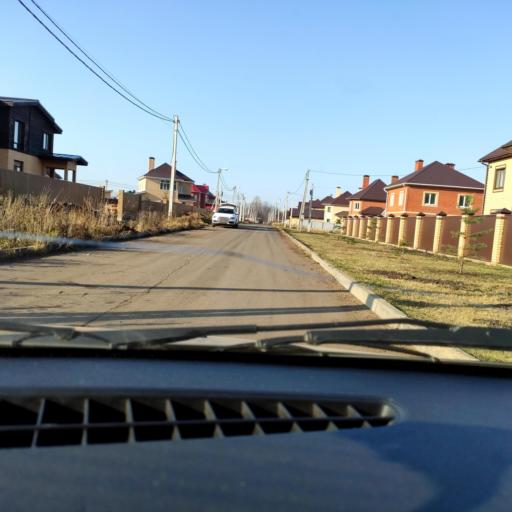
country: RU
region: Bashkortostan
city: Kabakovo
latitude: 54.6208
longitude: 56.1421
